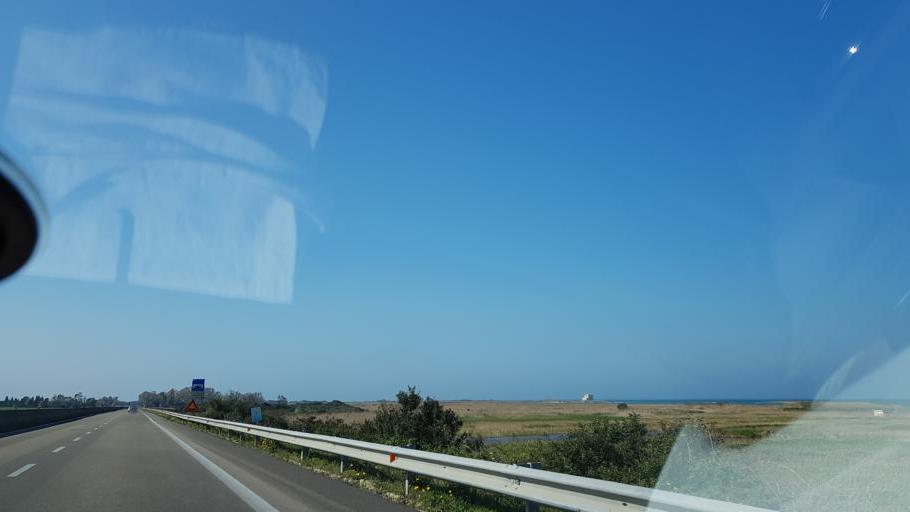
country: IT
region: Apulia
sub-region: Provincia di Brindisi
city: San Vito dei Normanni
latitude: 40.6998
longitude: 17.8066
